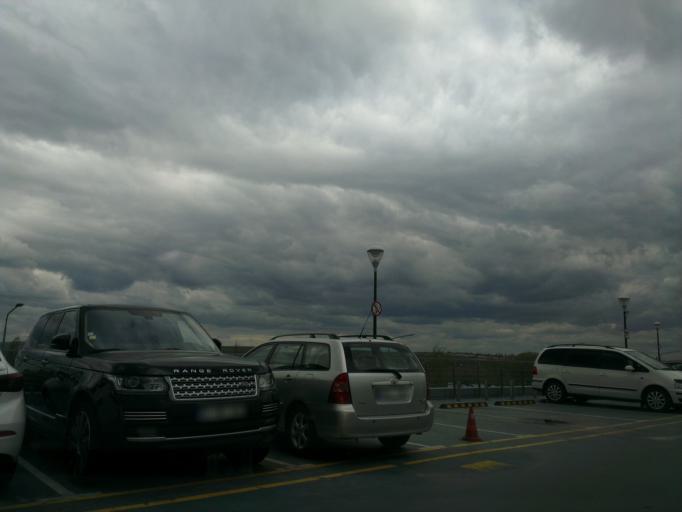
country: MD
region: Chisinau
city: Singera
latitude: 46.9359
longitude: 28.9350
